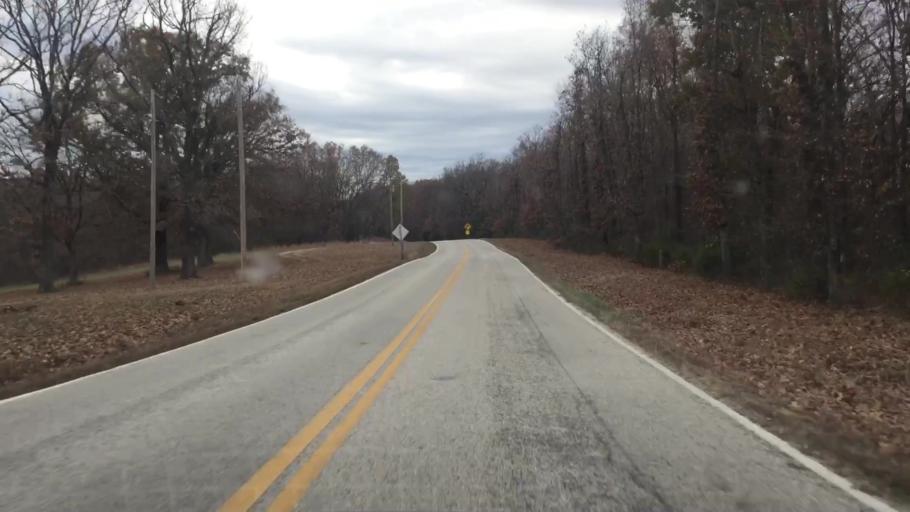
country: US
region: Missouri
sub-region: Saint Clair County
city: Osceola
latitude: 37.9876
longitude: -93.6378
